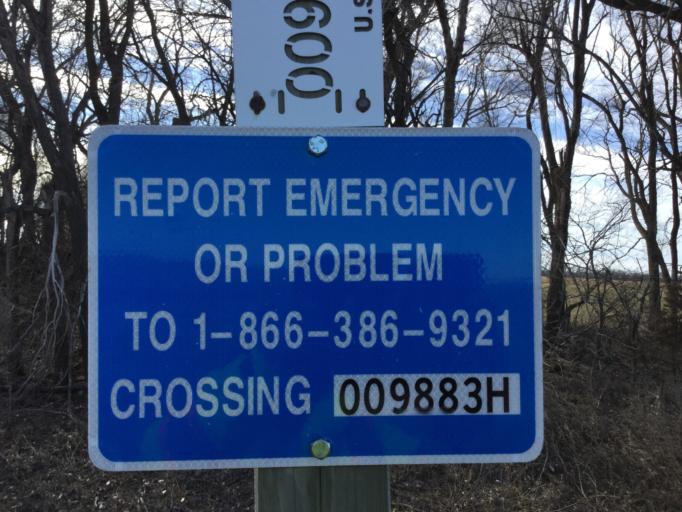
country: US
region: Kansas
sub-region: Rice County
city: Sterling
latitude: 38.2315
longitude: -98.2802
